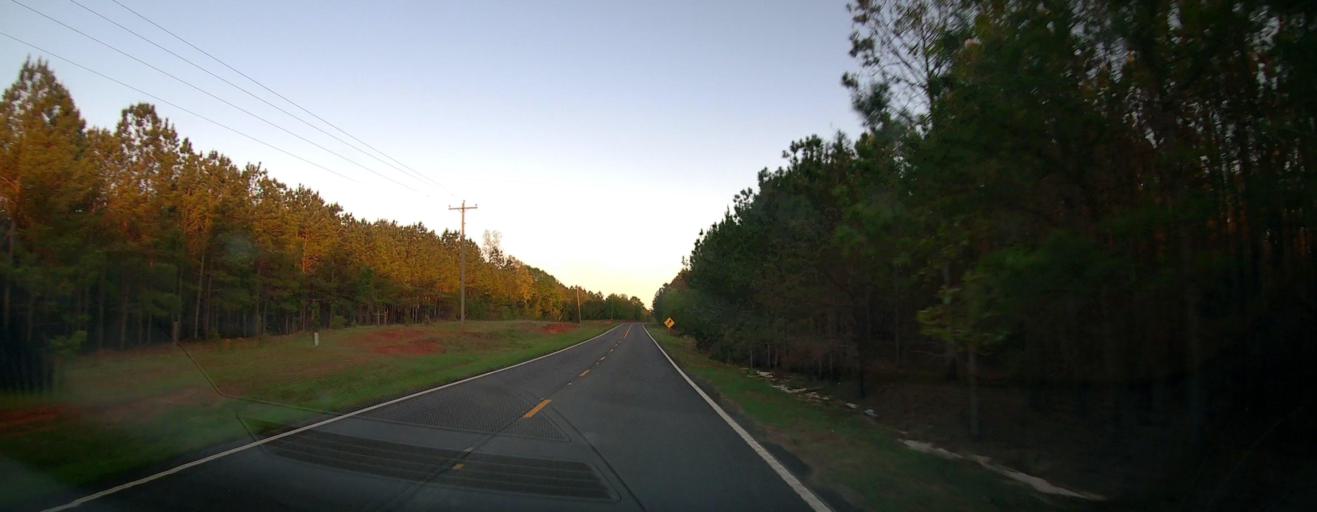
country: US
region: Georgia
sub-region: Marion County
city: Buena Vista
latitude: 32.3918
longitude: -84.5693
